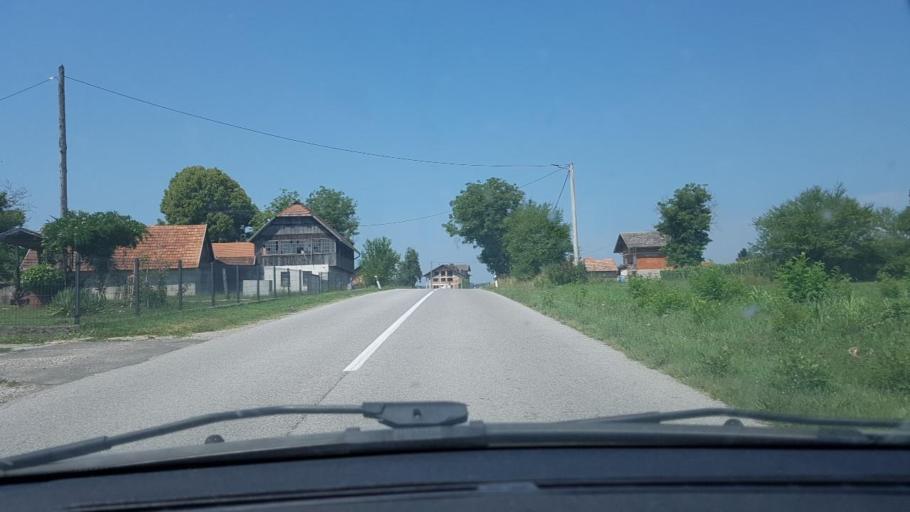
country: BA
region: Federation of Bosnia and Herzegovina
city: Velika Kladusa
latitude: 45.2139
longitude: 15.7653
